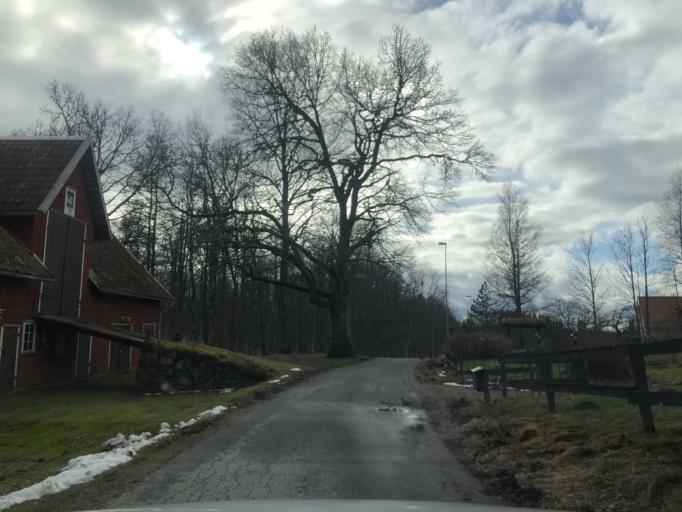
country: SE
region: Vaestra Goetaland
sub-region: Ulricehamns Kommun
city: Ulricehamn
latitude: 57.7703
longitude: 13.4177
